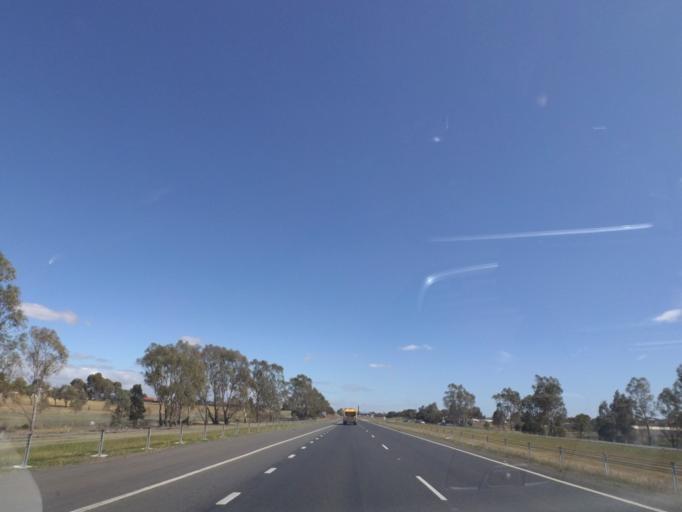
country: AU
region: Victoria
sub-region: Melton
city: Brookfield
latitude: -37.6896
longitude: 144.5600
